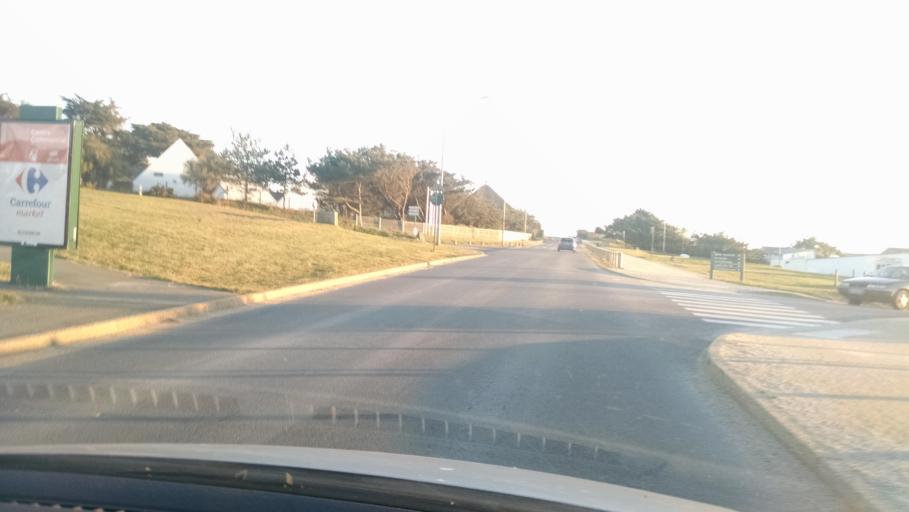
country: FR
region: Brittany
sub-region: Departement du Morbihan
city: Guidel-Plage
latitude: 47.7676
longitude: -3.5242
